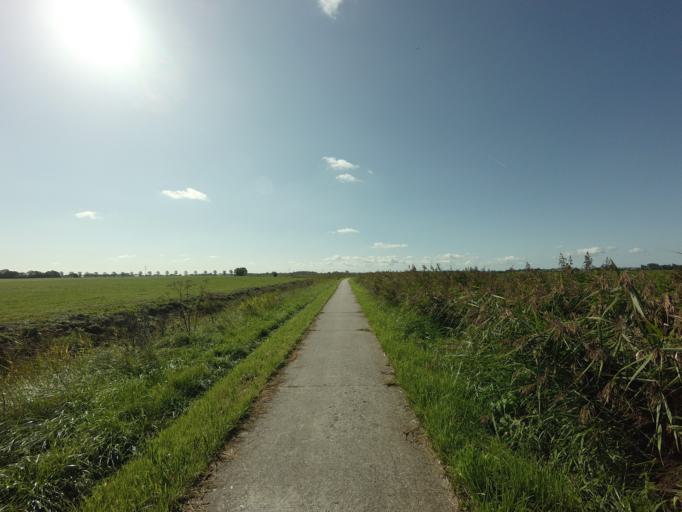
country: NL
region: Friesland
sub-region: Gemeente Boarnsterhim
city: Reduzum
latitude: 53.1256
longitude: 5.7551
